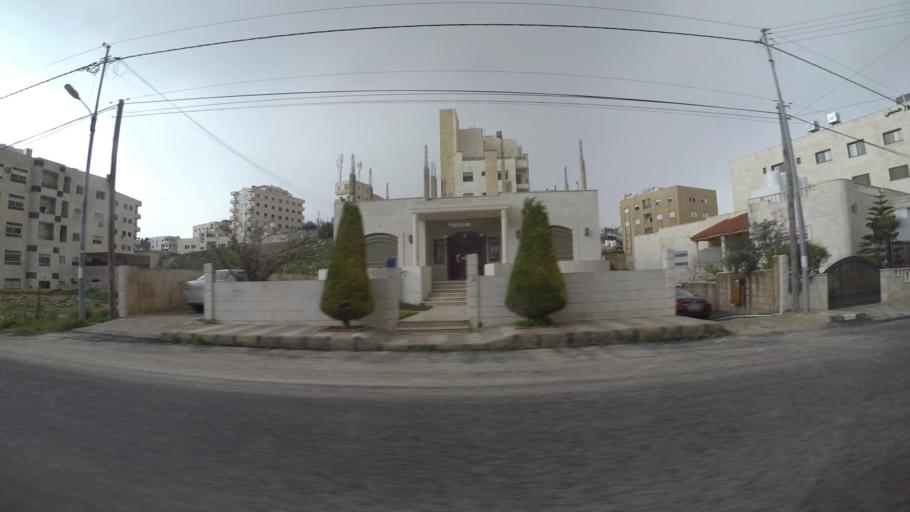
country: JO
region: Amman
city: Umm as Summaq
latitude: 31.8812
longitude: 35.8538
